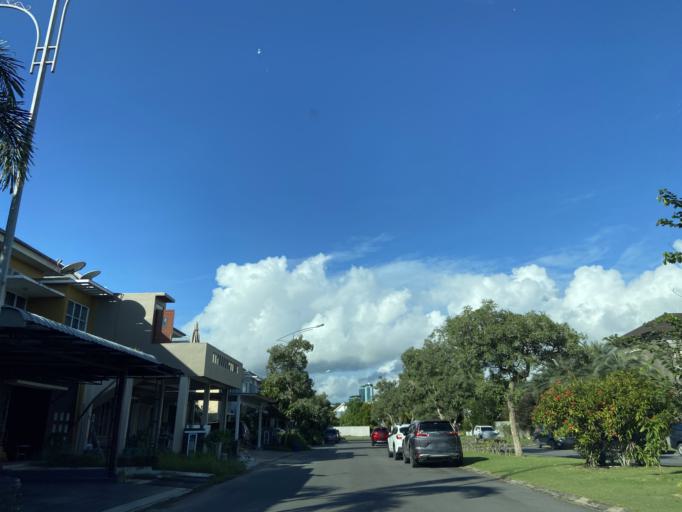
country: SG
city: Singapore
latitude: 1.0937
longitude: 104.0340
